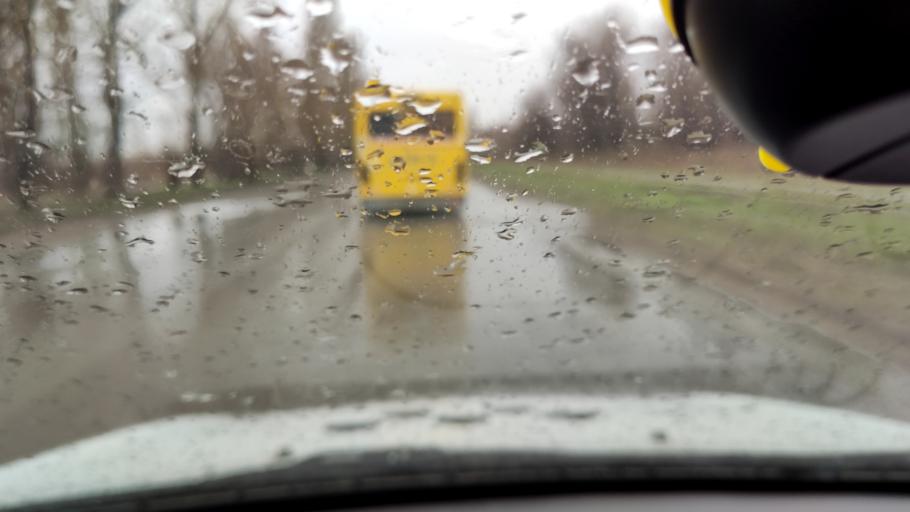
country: RU
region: Samara
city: Podstepki
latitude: 53.5770
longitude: 49.2195
